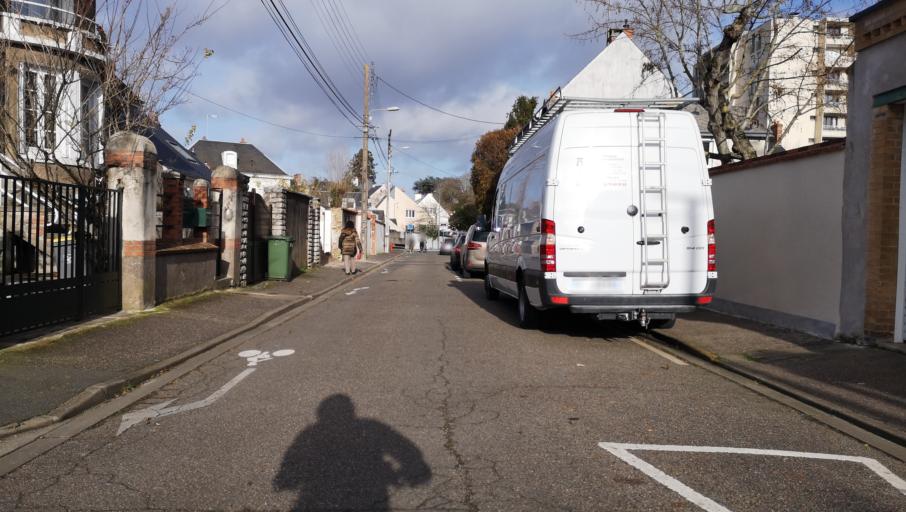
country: FR
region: Centre
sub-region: Departement du Loiret
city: Saint-Jean-le-Blanc
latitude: 47.8907
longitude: 1.9039
